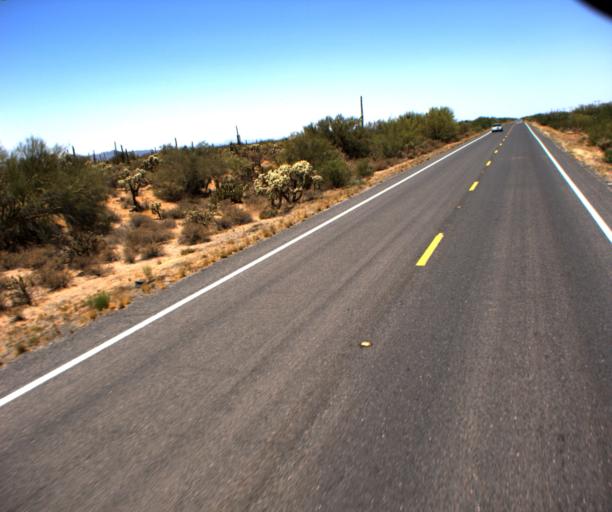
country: US
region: Arizona
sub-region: Pinal County
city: Florence
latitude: 32.8183
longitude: -111.1999
